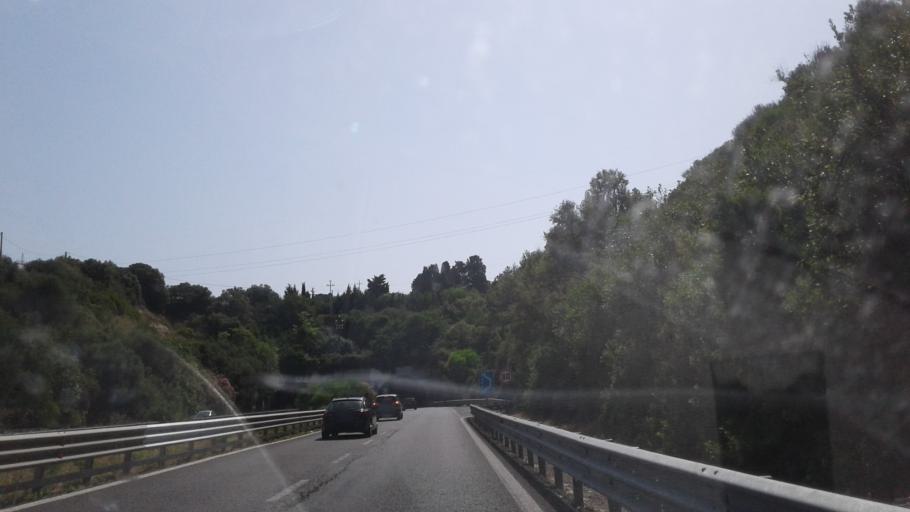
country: IT
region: Sardinia
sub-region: Provincia di Sassari
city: Tissi
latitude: 40.6980
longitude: 8.5667
